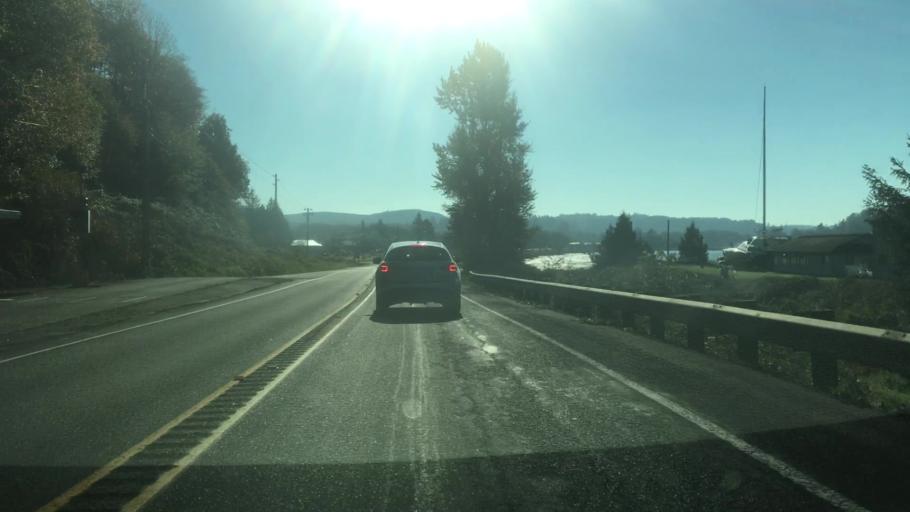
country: US
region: Washington
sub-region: Pacific County
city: Raymond
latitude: 46.6793
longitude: -123.7598
